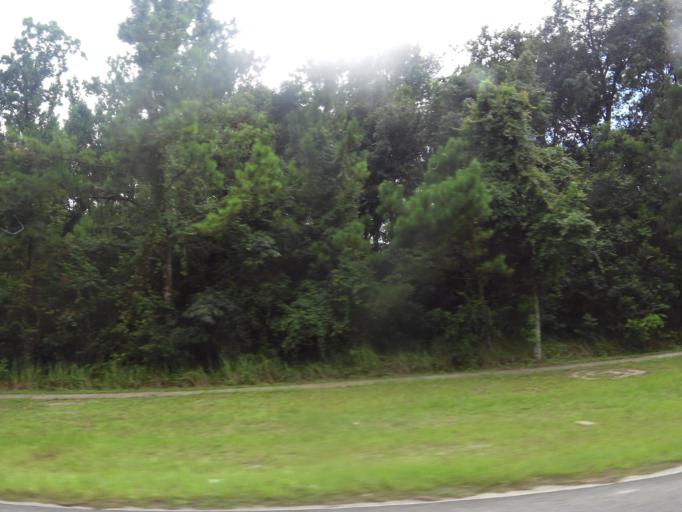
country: US
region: Florida
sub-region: Duval County
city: Jacksonville
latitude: 30.2795
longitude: -81.5697
